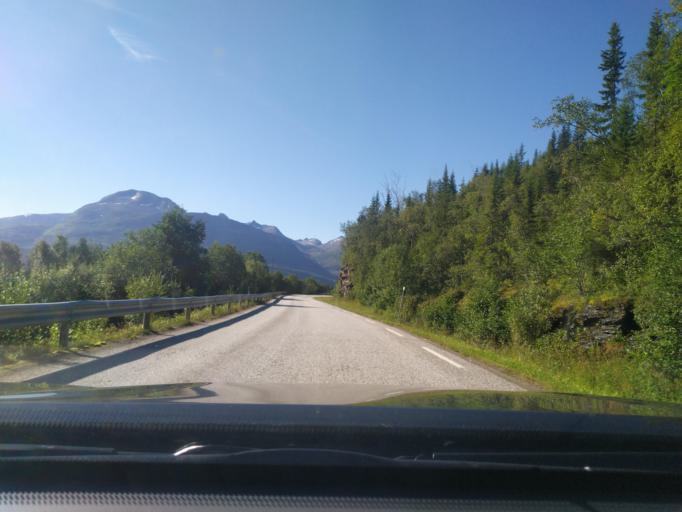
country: NO
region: Troms
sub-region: Dyroy
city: Brostadbotn
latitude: 68.9260
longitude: 17.6400
